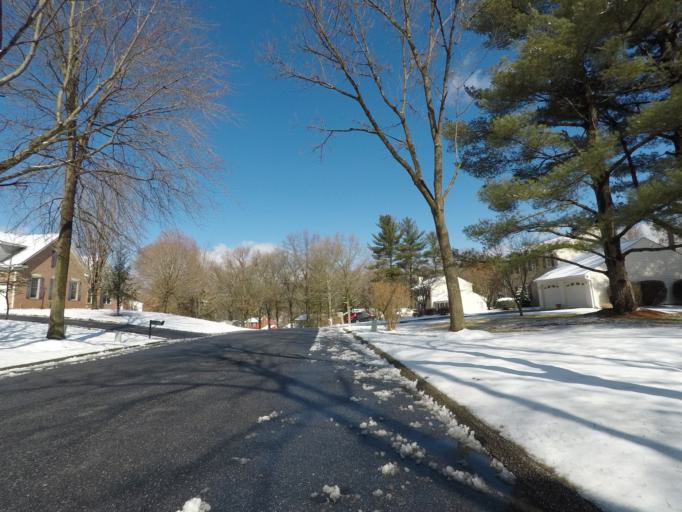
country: US
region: Maryland
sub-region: Howard County
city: Columbia
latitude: 39.2692
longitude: -76.8541
